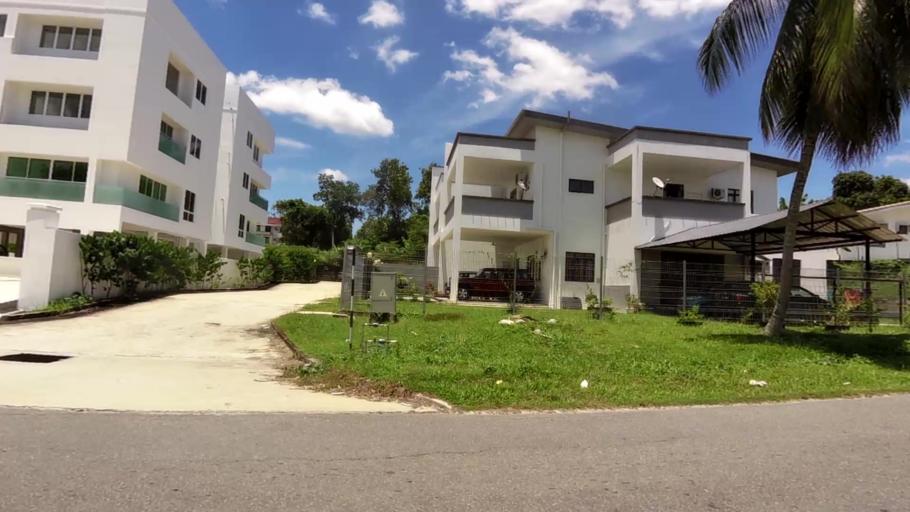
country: BN
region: Brunei and Muara
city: Bandar Seri Begawan
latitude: 4.9452
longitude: 114.9594
